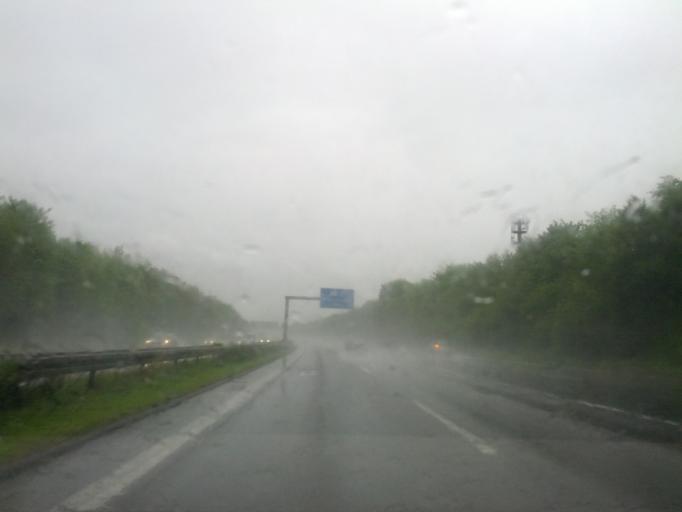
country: DE
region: North Rhine-Westphalia
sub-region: Regierungsbezirk Koln
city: Neustadt/Sued
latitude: 50.8891
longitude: 6.9301
